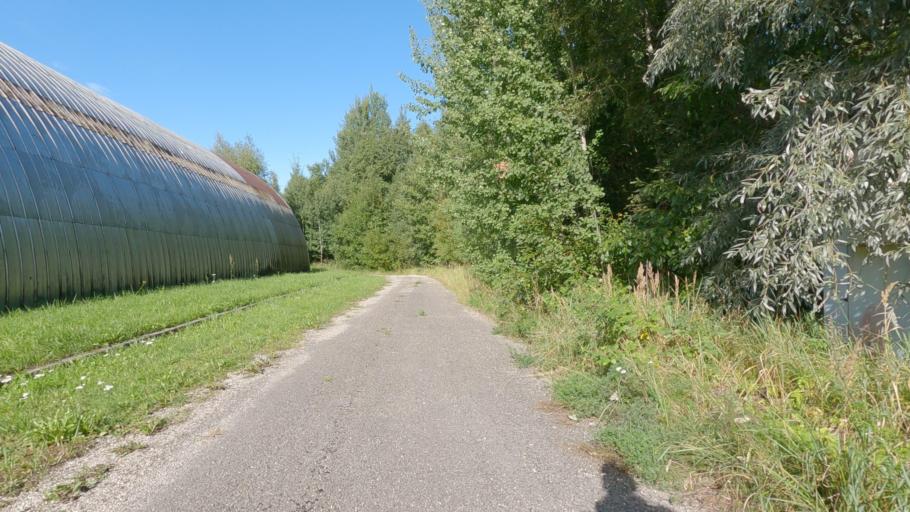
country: EE
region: Raplamaa
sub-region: Rapla vald
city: Rapla
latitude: 58.9969
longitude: 24.8278
